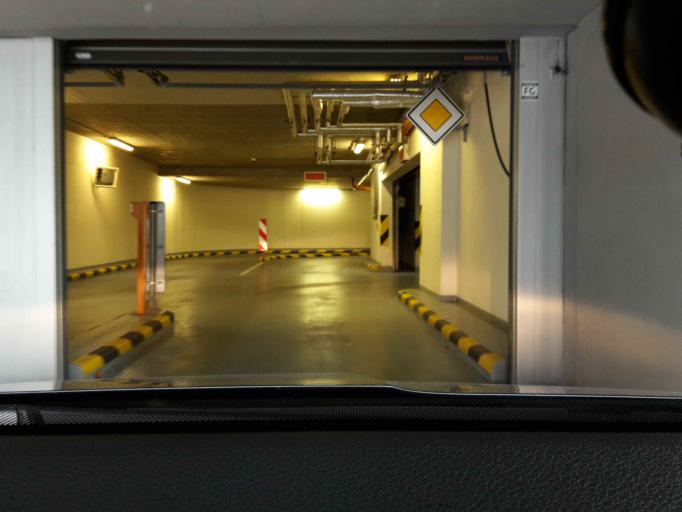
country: CZ
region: Central Bohemia
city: Hostivice
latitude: 50.0479
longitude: 14.3041
